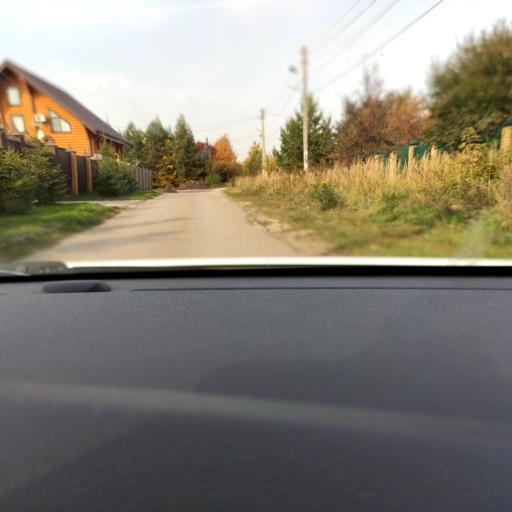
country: RU
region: Tatarstan
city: Vysokaya Gora
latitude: 55.8099
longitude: 49.2447
